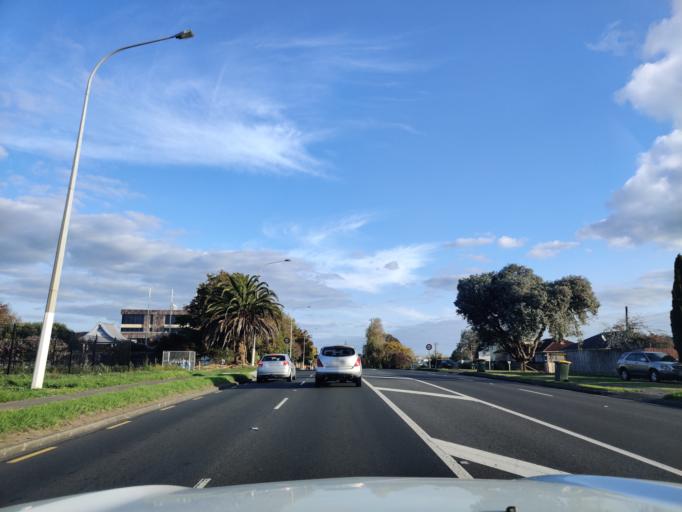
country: NZ
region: Auckland
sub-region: Auckland
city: Manukau City
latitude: -36.9518
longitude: 174.8915
